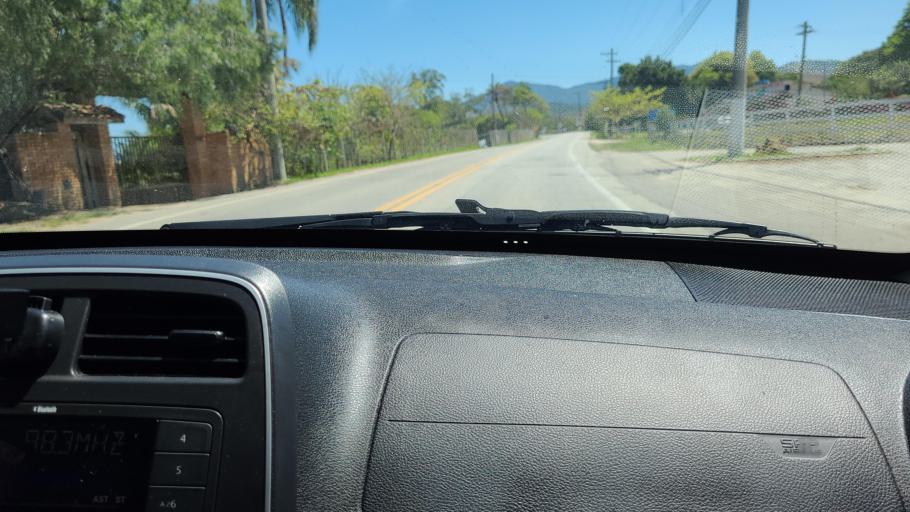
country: BR
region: Sao Paulo
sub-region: Pindamonhangaba
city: Pindamonhangaba
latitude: -22.8854
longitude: -45.5180
